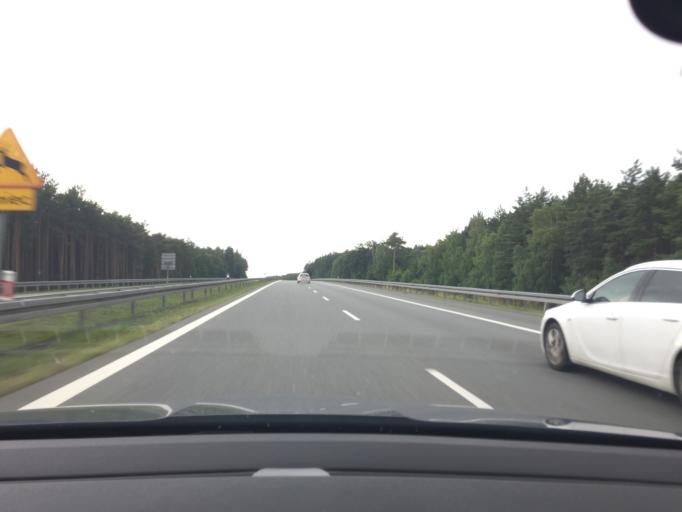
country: PL
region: Greater Poland Voivodeship
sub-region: Powiat nowotomyski
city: Nowy Tomysl
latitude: 52.3676
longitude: 16.1771
